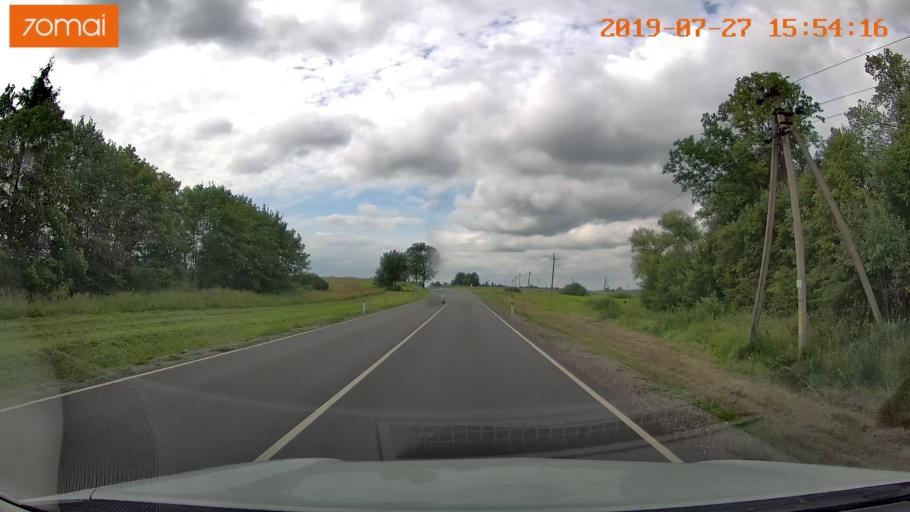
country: RU
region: Kaliningrad
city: Chernyakhovsk
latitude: 54.6066
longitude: 21.9415
